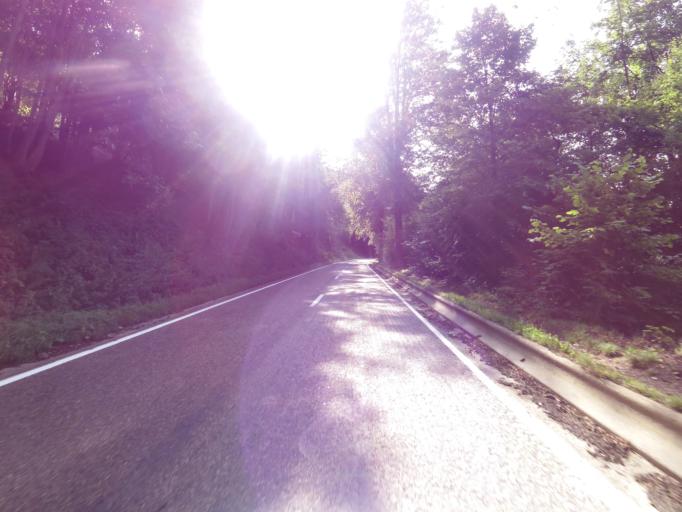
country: BE
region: Wallonia
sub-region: Province du Luxembourg
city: La Roche-en-Ardenne
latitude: 50.1929
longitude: 5.5746
